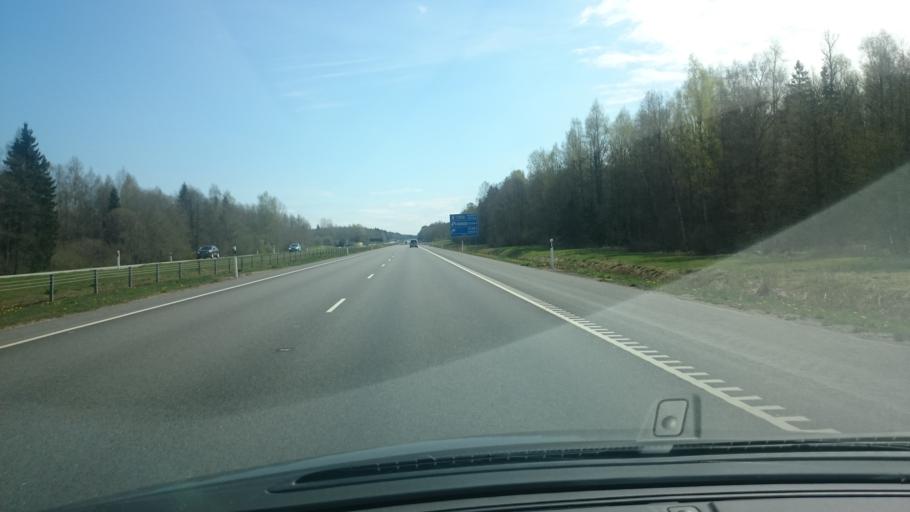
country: EE
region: Harju
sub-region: Loksa linn
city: Loksa
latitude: 59.4635
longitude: 25.6958
